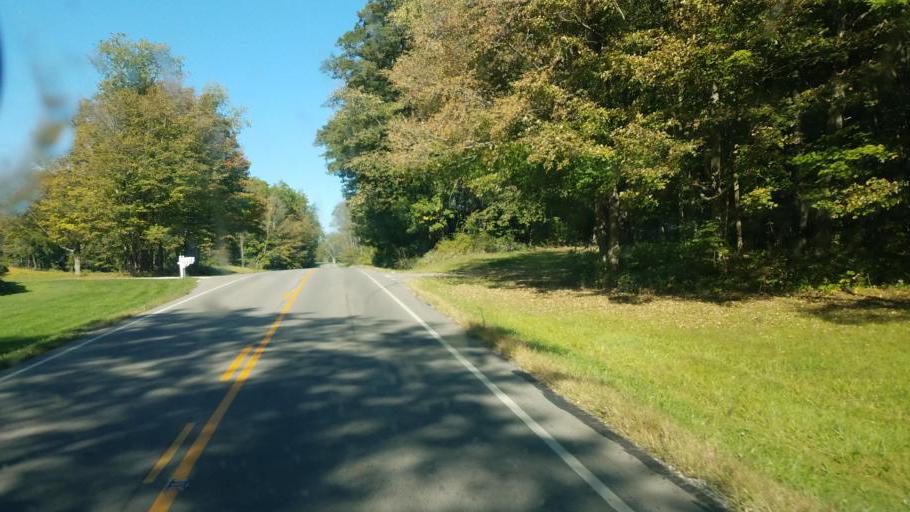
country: US
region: Ohio
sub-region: Richland County
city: Lexington
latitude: 40.7015
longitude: -82.6318
